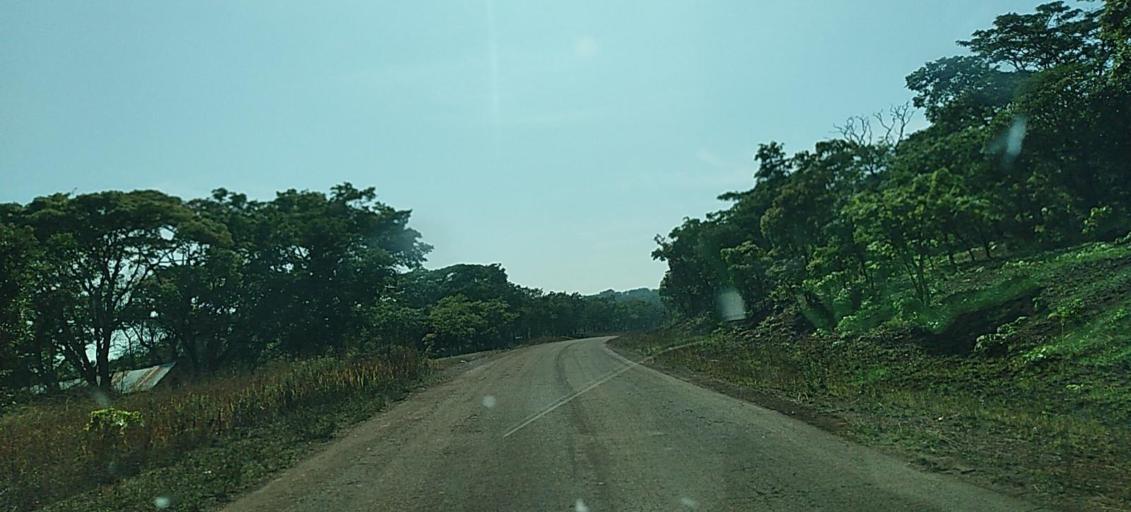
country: ZM
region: North-Western
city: Mwinilunga
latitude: -11.7848
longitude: 25.0416
